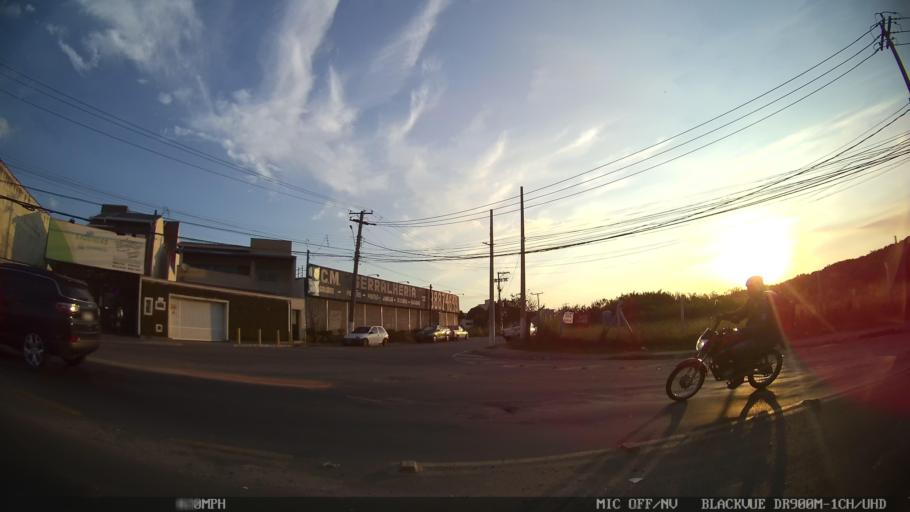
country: BR
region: Sao Paulo
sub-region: Hortolandia
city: Hortolandia
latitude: -22.8679
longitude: -47.2018
